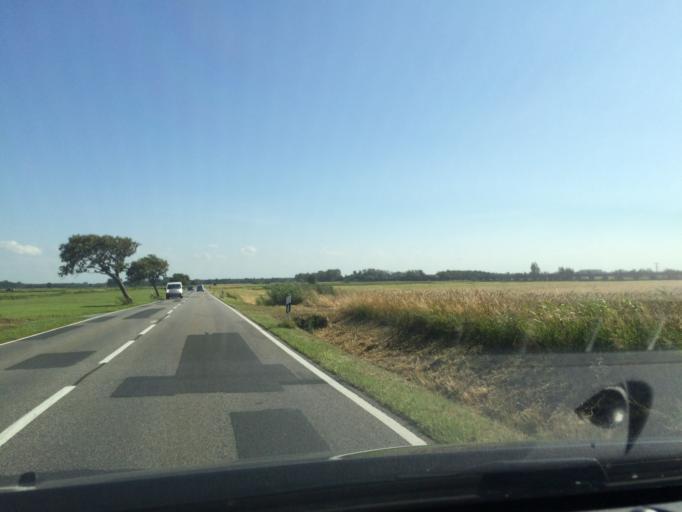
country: DE
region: Mecklenburg-Vorpommern
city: Zingst
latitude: 54.3977
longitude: 12.6774
